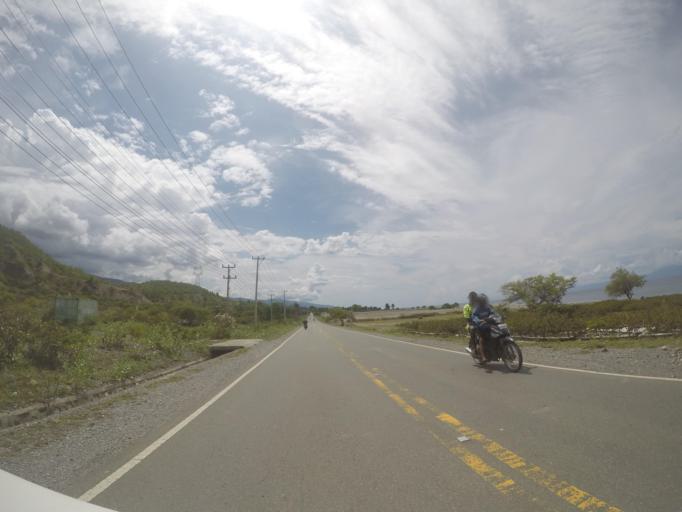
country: TL
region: Liquica
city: Liquica
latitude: -8.5772
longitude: 125.3689
